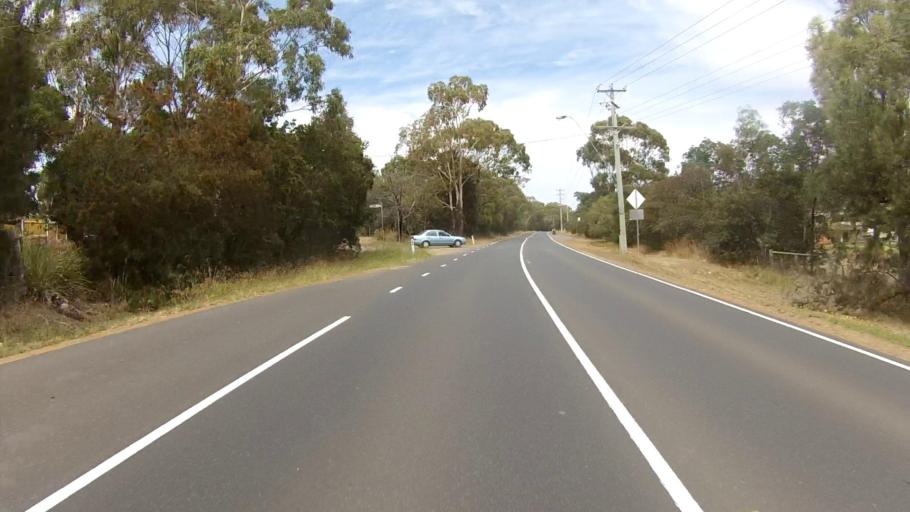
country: AU
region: Tasmania
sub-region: Clarence
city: Acton Park
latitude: -42.8746
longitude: 147.4830
